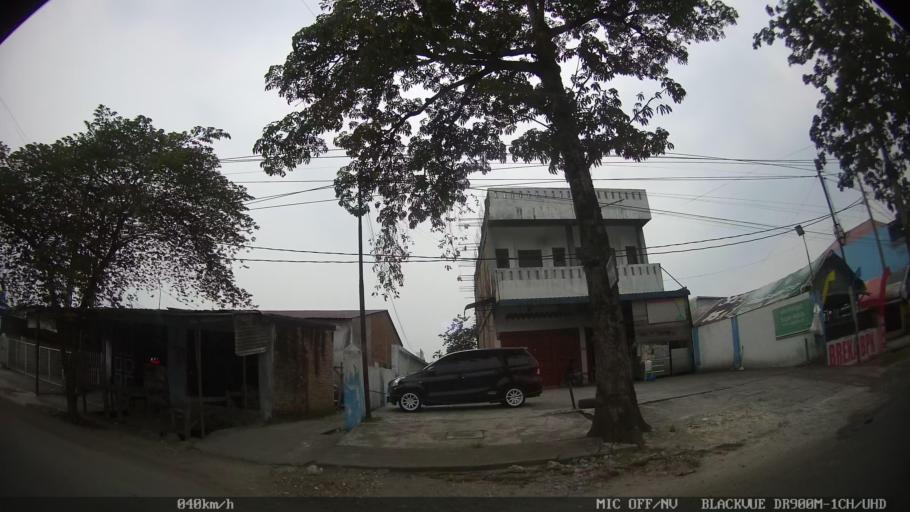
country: ID
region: North Sumatra
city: Medan
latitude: 3.5547
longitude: 98.7030
